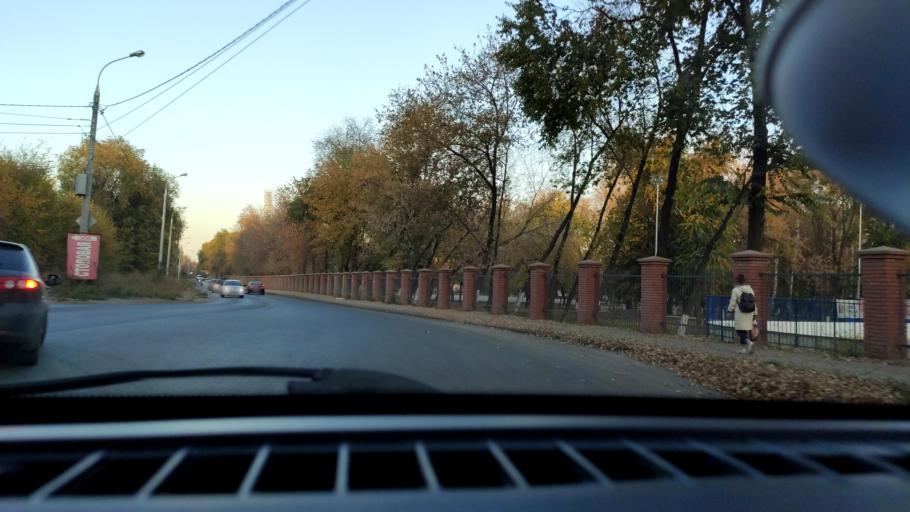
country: RU
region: Samara
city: Petra-Dubrava
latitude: 53.2368
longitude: 50.2648
